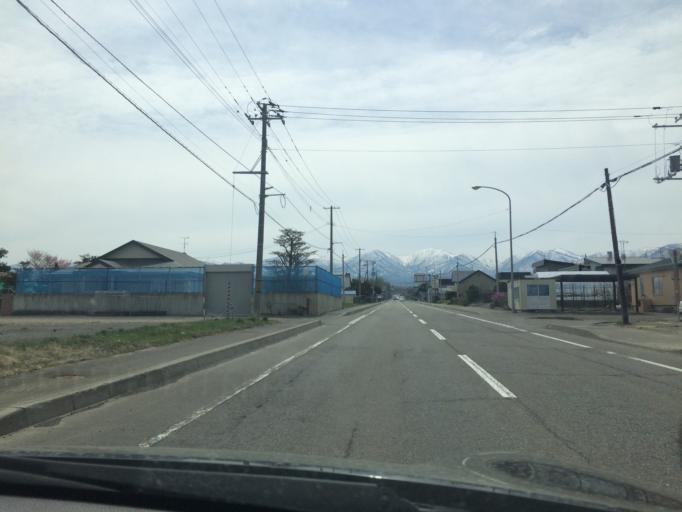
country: JP
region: Hokkaido
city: Otofuke
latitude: 43.0154
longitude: 142.8921
